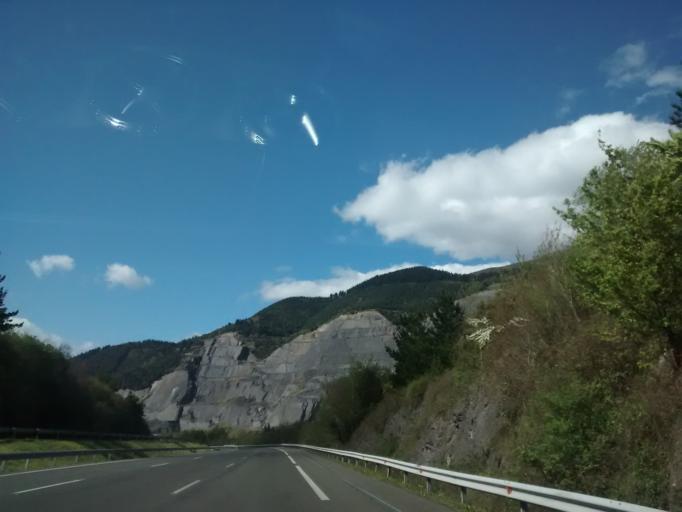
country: ES
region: Basque Country
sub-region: Bizkaia
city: Elexalde
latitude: 43.1190
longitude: -2.9157
